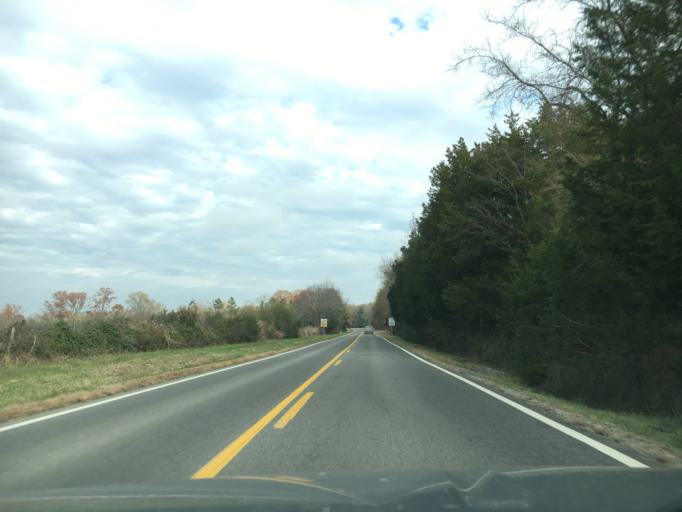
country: US
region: Virginia
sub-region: Prince Edward County
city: Farmville
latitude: 37.4026
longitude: -78.3653
